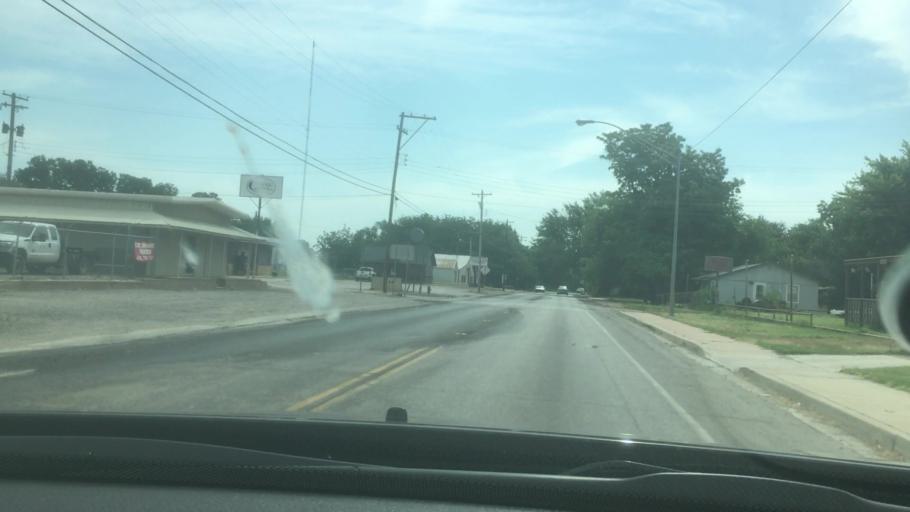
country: US
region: Oklahoma
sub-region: Garvin County
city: Maysville
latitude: 34.8172
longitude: -97.4048
